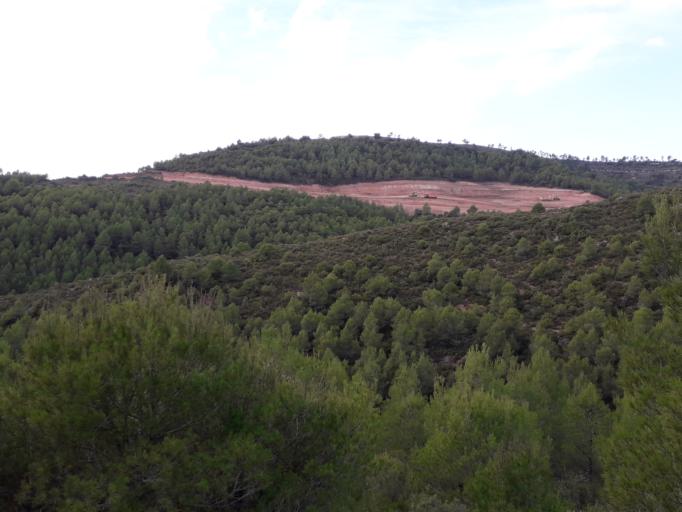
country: ES
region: Catalonia
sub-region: Provincia de Lleida
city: Sant Guim de Freixenet
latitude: 41.6113
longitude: 1.4758
